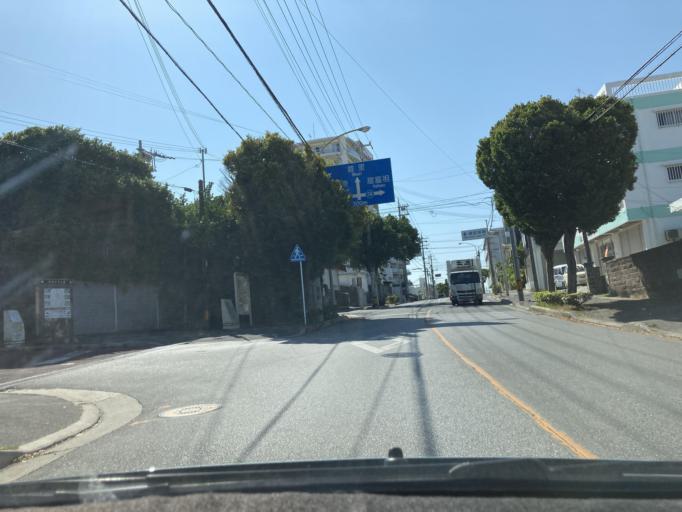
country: JP
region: Okinawa
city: Ginowan
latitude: 26.2497
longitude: 127.7264
